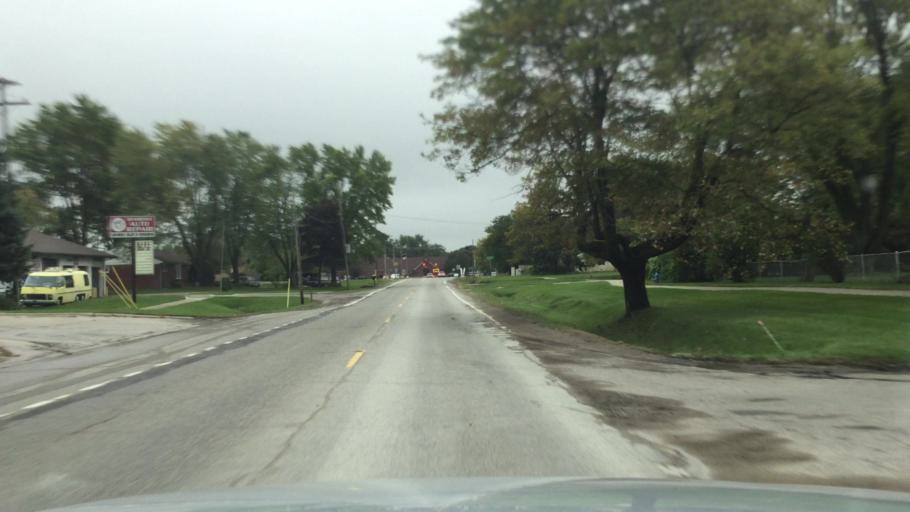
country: US
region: Michigan
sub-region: Oakland County
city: Waterford
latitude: 42.6924
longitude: -83.4075
